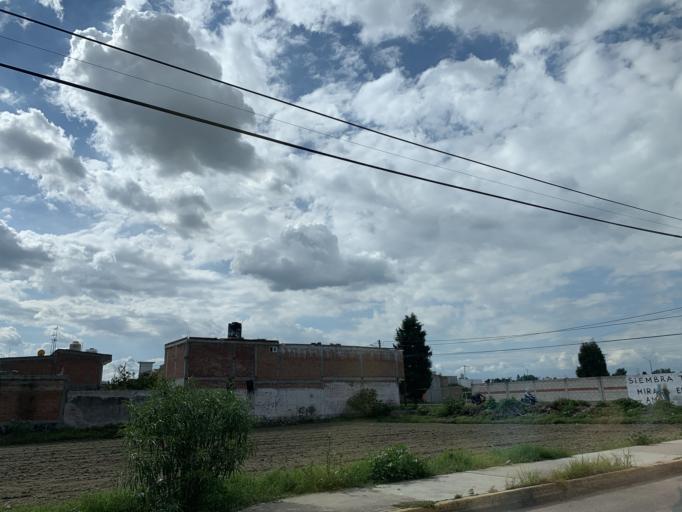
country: MX
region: Puebla
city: Cholula
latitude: 19.0643
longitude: -98.3177
